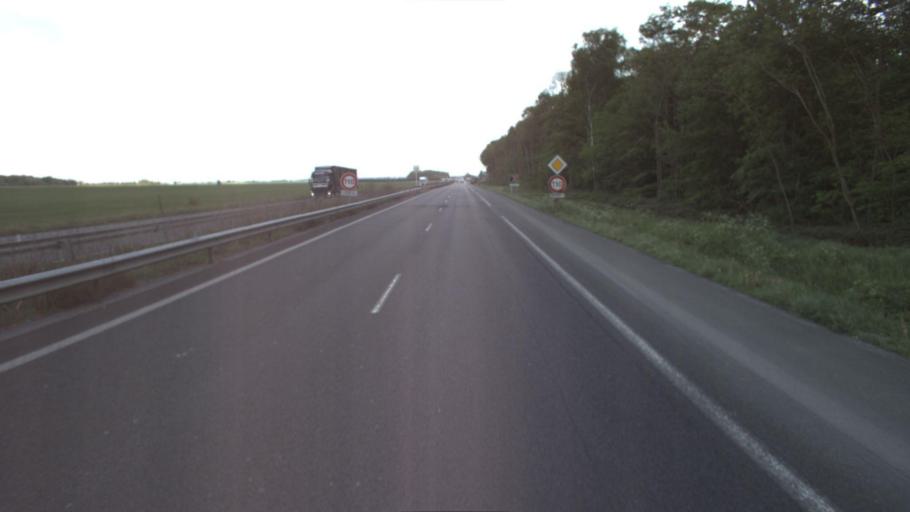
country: FR
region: Ile-de-France
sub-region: Departement de Seine-et-Marne
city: Fontenay-Tresigny
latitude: 48.6946
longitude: 2.9077
